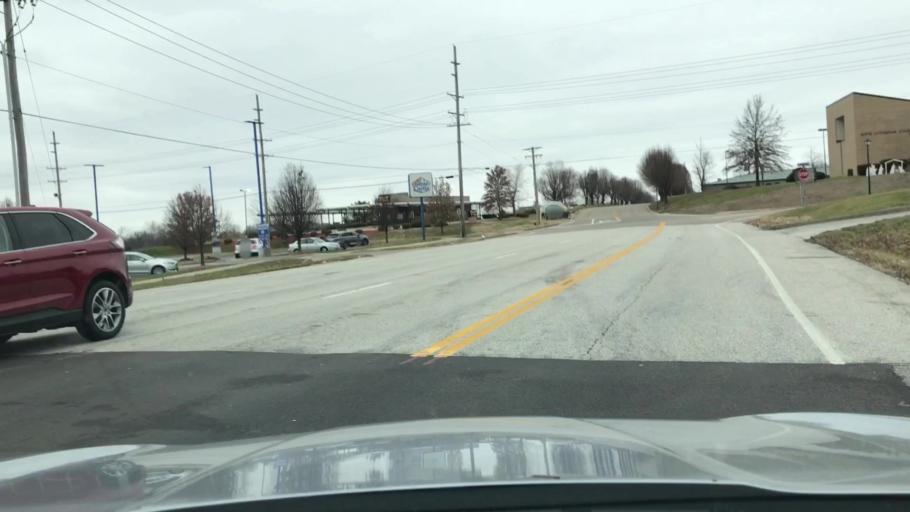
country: US
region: Missouri
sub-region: Saint Charles County
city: Saint Charles
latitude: 38.7614
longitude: -90.5303
